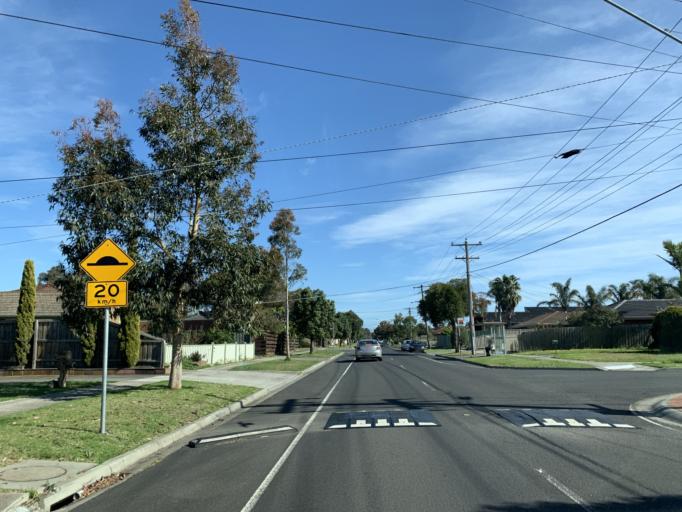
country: AU
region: Victoria
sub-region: Brimbank
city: Kealba
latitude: -37.7373
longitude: 144.8278
